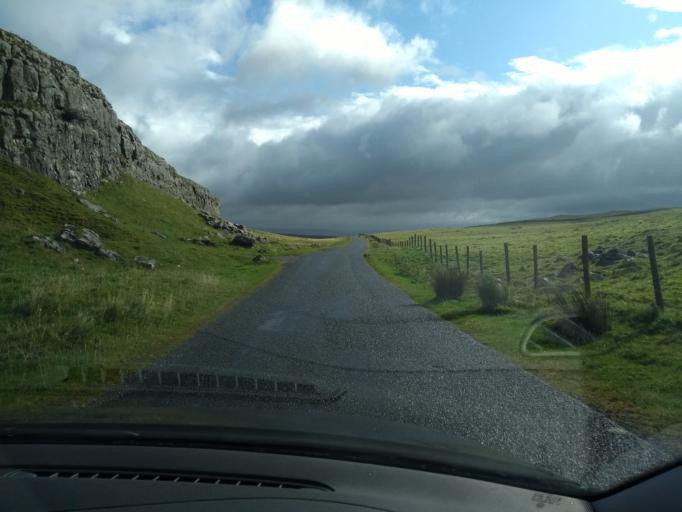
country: GB
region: England
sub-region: North Yorkshire
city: Settle
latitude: 54.0833
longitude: -2.1780
